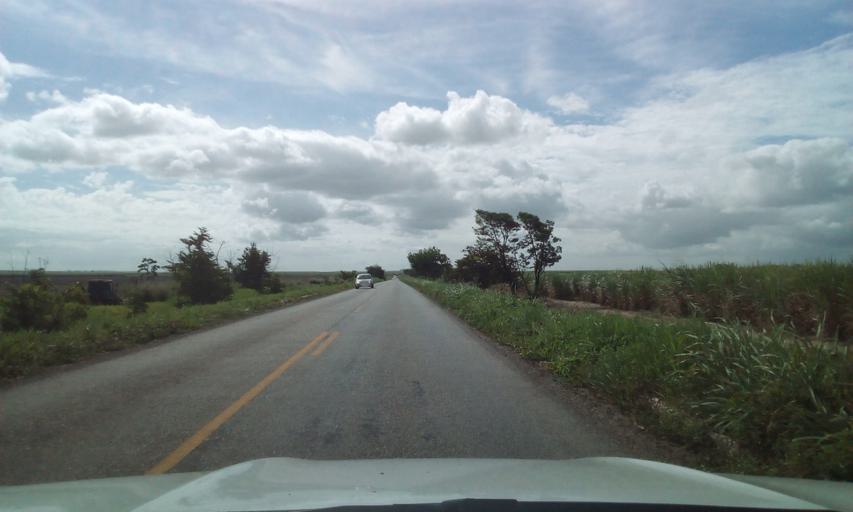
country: BR
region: Paraiba
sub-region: Santa Rita
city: Santa Rita
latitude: -7.0787
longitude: -34.9848
